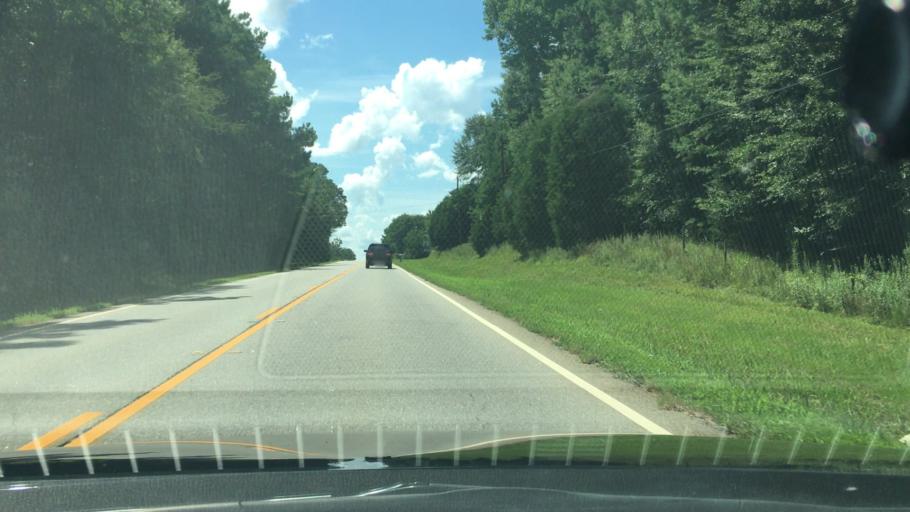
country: US
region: Georgia
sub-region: Putnam County
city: Eatonton
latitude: 33.3074
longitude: -83.4929
